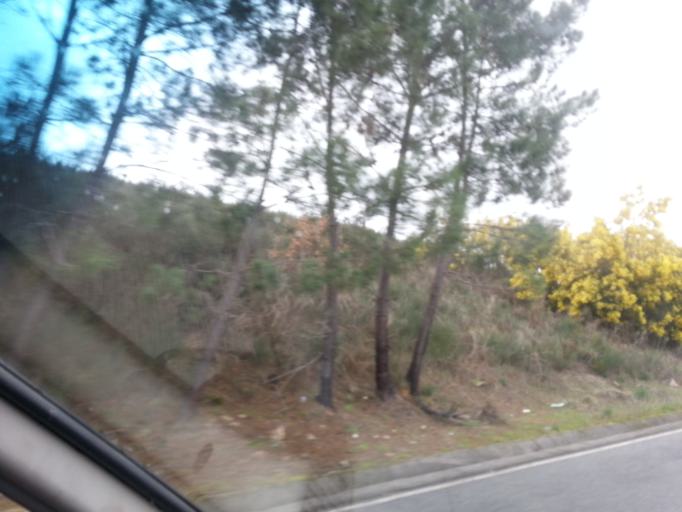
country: PT
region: Viseu
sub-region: Viseu
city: Rio de Loba
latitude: 40.6151
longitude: -7.8653
